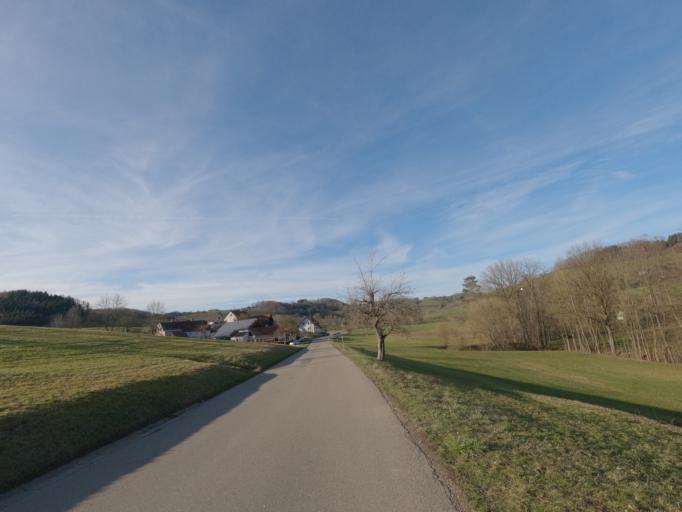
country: DE
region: Baden-Wuerttemberg
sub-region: Regierungsbezirk Stuttgart
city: Donzdorf
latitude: 48.7117
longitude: 9.7917
